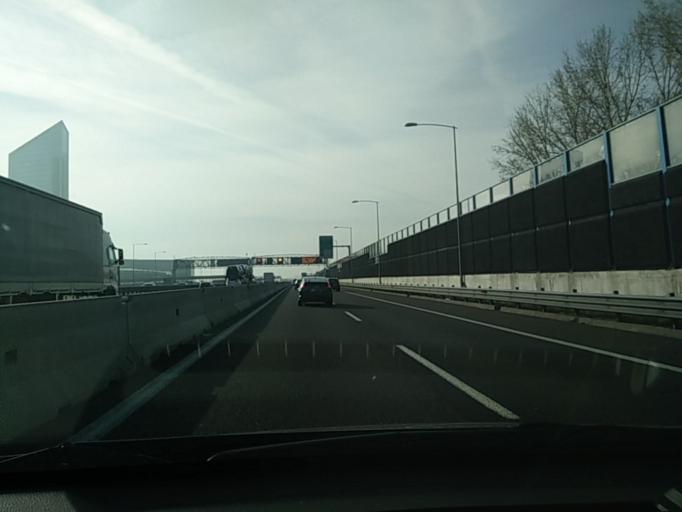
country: IT
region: Emilia-Romagna
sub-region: Provincia di Bologna
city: San Lazzaro
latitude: 44.4984
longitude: 11.3866
